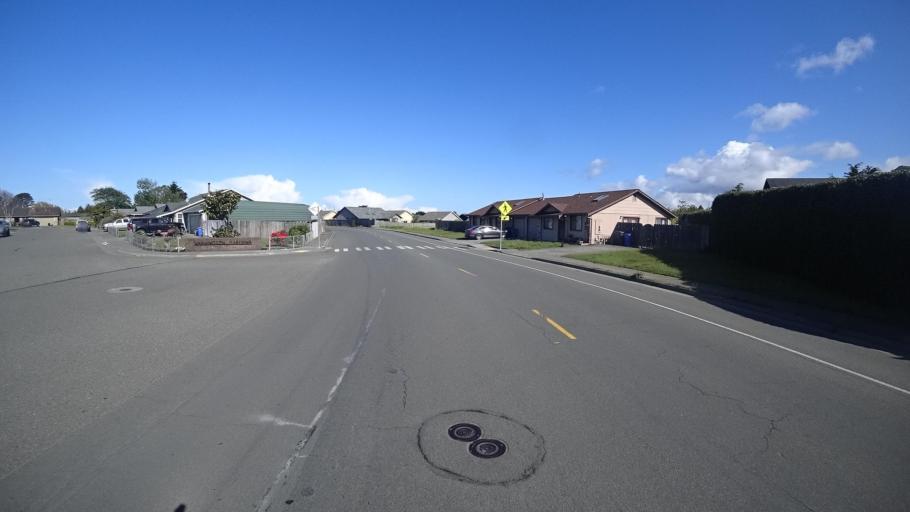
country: US
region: California
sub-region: Humboldt County
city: McKinleyville
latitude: 40.9375
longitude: -124.1080
